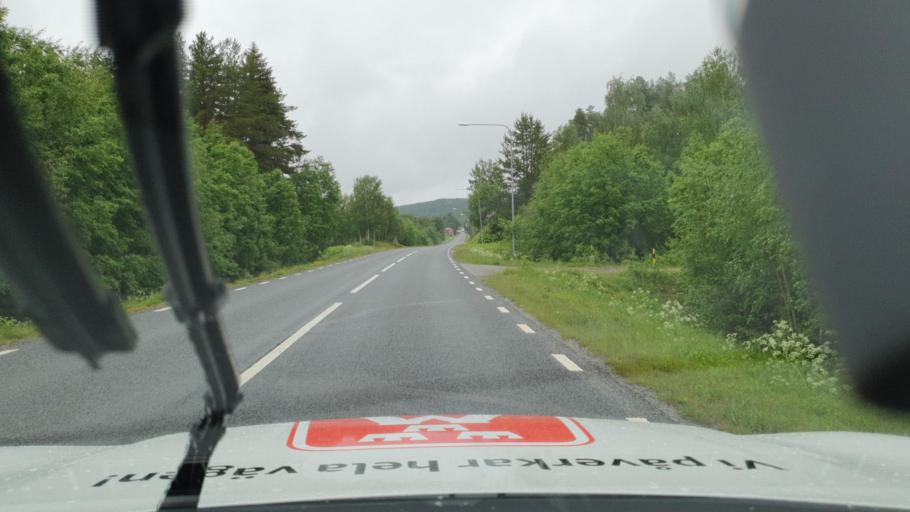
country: SE
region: Vaesterbotten
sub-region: Asele Kommun
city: Asele
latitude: 63.9330
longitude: 17.2695
